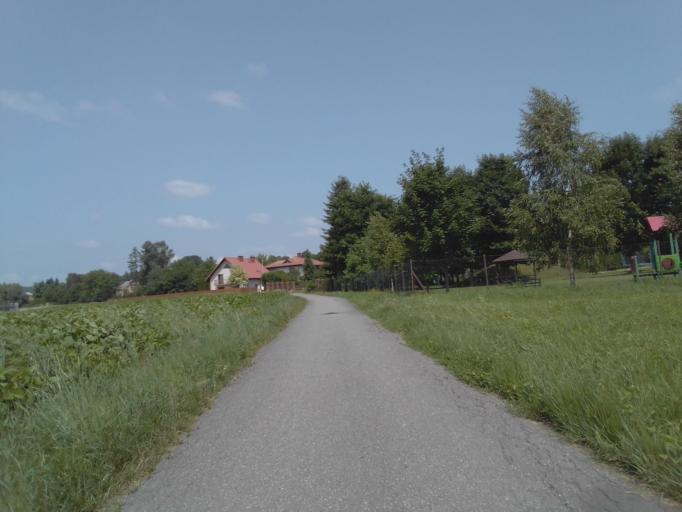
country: PL
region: Subcarpathian Voivodeship
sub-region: Powiat strzyzowski
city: Czudec
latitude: 49.9434
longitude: 21.8353
